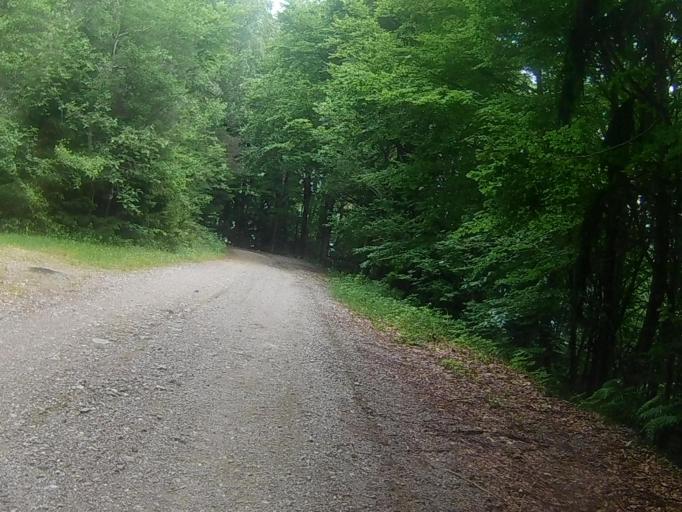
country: SI
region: Maribor
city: Limbus
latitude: 46.5227
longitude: 15.5741
